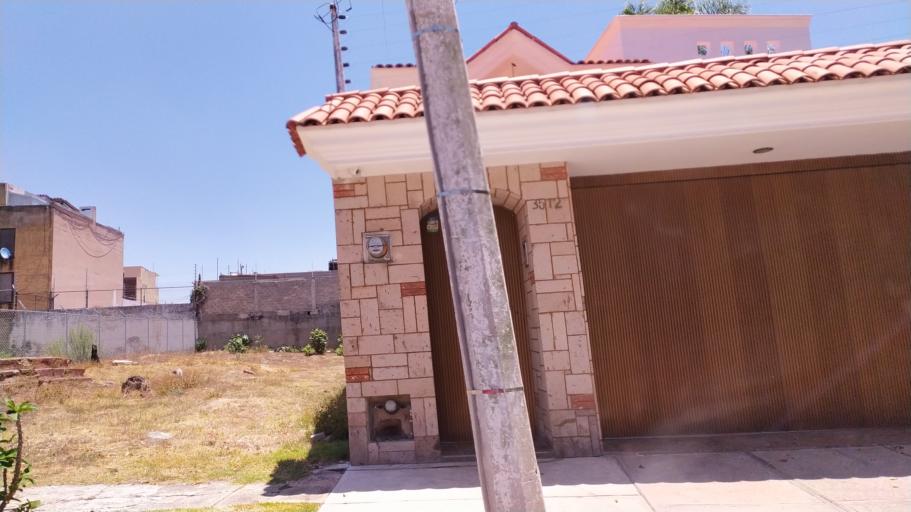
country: MX
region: Jalisco
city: Guadalajara
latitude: 20.6823
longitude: -103.4013
